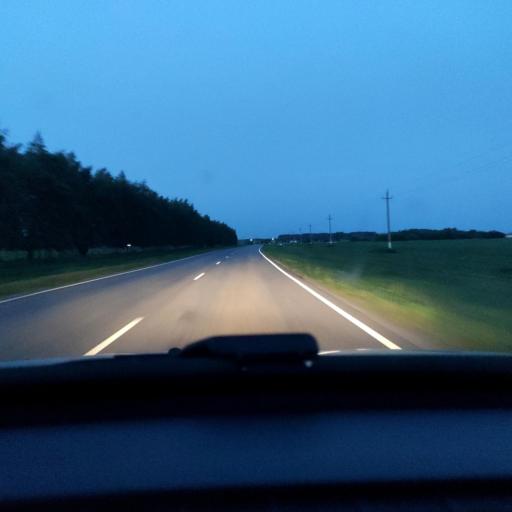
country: RU
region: Voronezj
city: Panino
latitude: 51.6544
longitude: 40.0058
